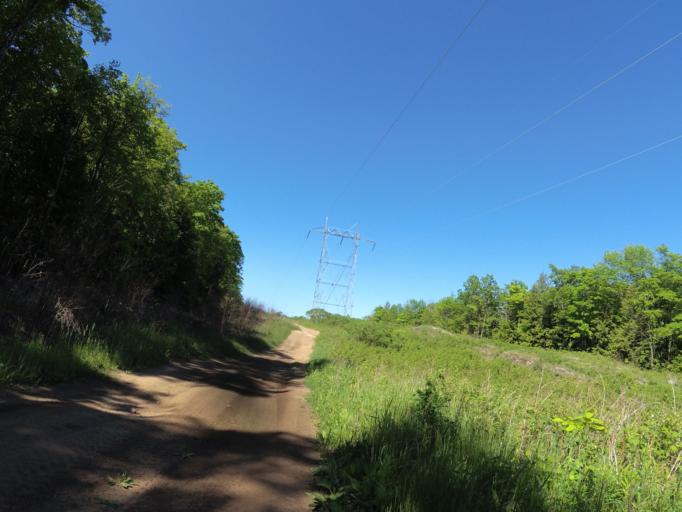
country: CA
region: Ontario
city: Renfrew
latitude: 45.0917
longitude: -77.0781
